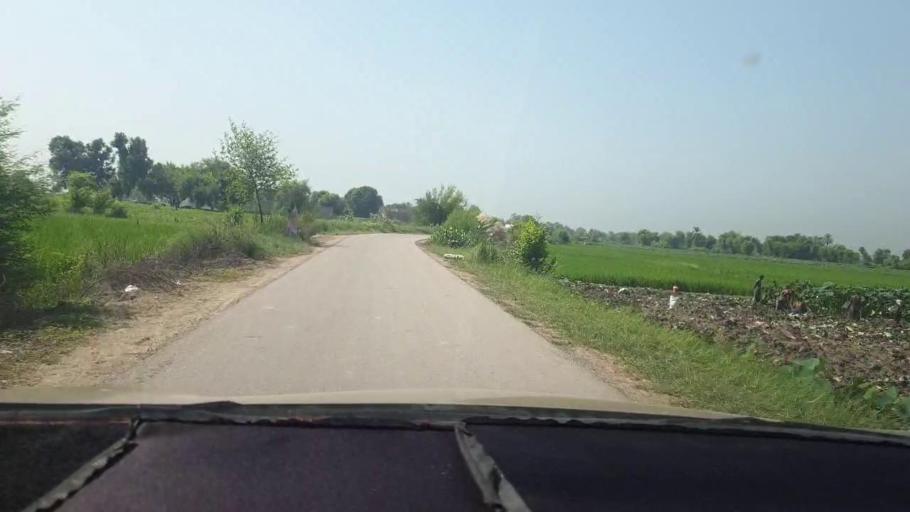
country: PK
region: Sindh
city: Kambar
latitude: 27.5831
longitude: 68.0475
